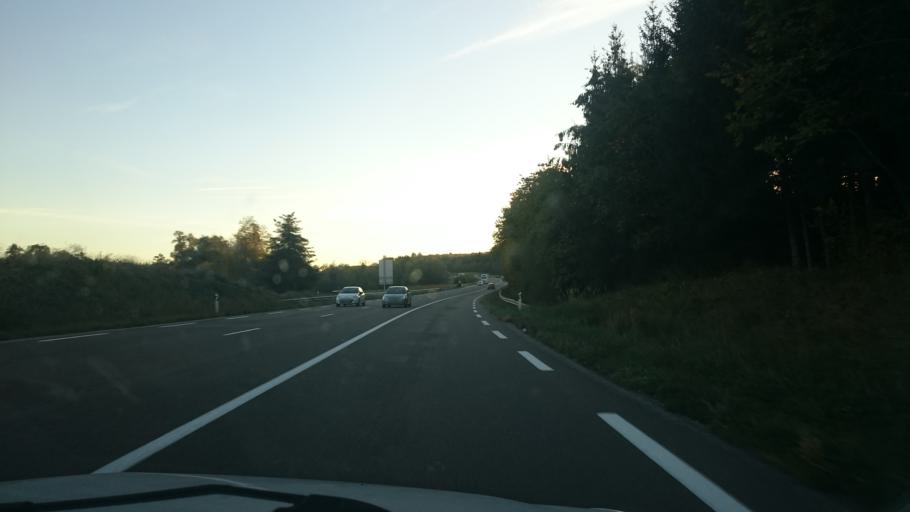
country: FR
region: Franche-Comte
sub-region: Departement du Jura
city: Mouchard
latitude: 46.9551
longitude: 5.7883
